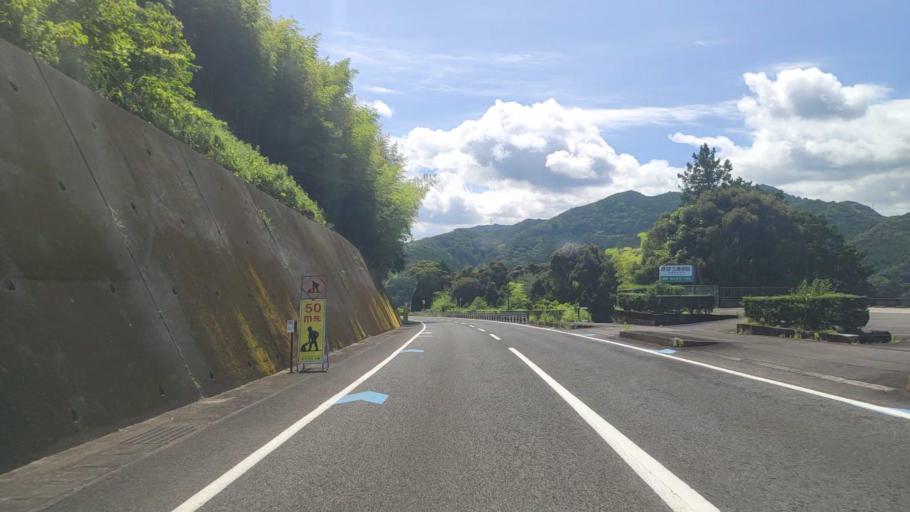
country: JP
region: Wakayama
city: Shingu
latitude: 33.7456
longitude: 136.0128
